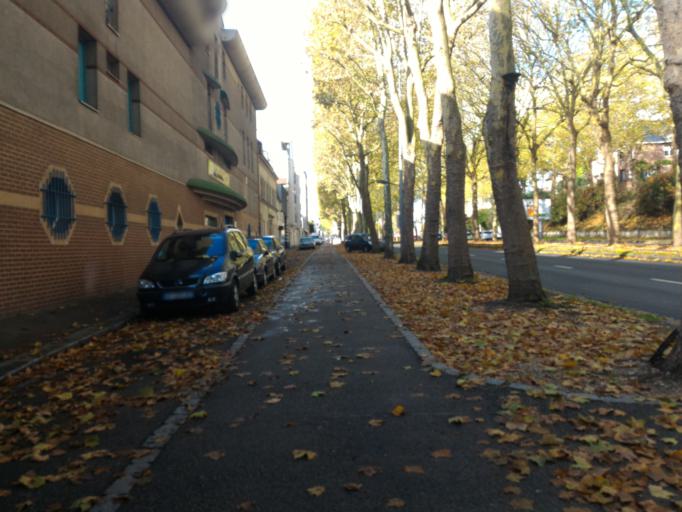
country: FR
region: Haute-Normandie
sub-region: Departement de la Seine-Maritime
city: Rouen
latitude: 49.4449
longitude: 1.1103
